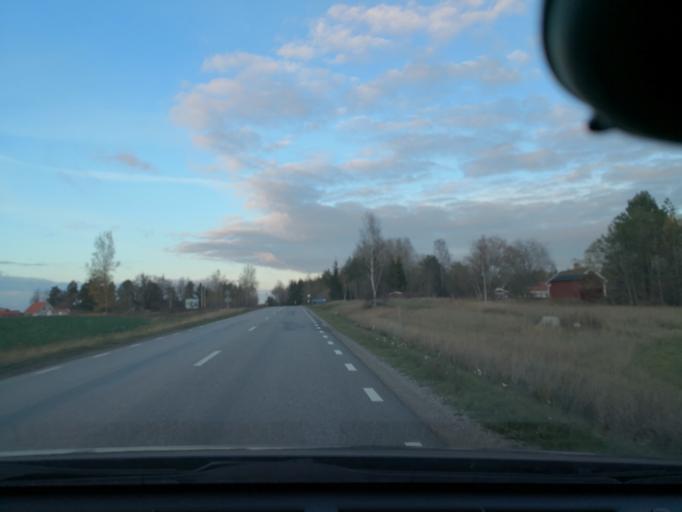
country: SE
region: Vaestmanland
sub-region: Vasteras
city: Tillberga
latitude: 59.6557
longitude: 16.6948
